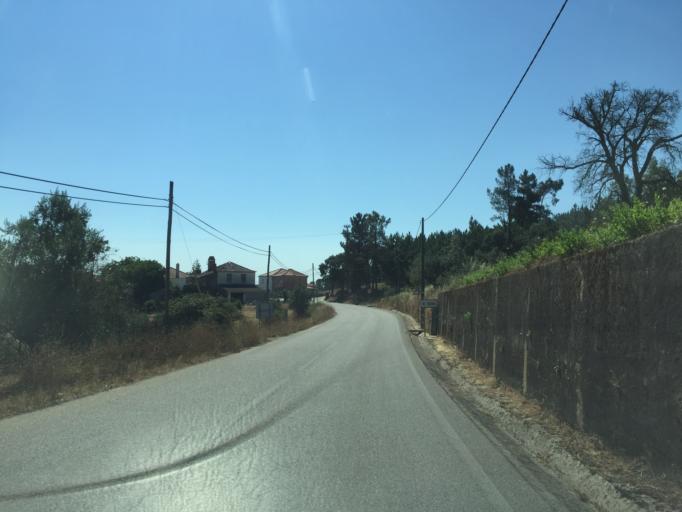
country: PT
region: Santarem
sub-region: Ferreira do Zezere
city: Ferreira do Zezere
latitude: 39.5978
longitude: -8.2982
